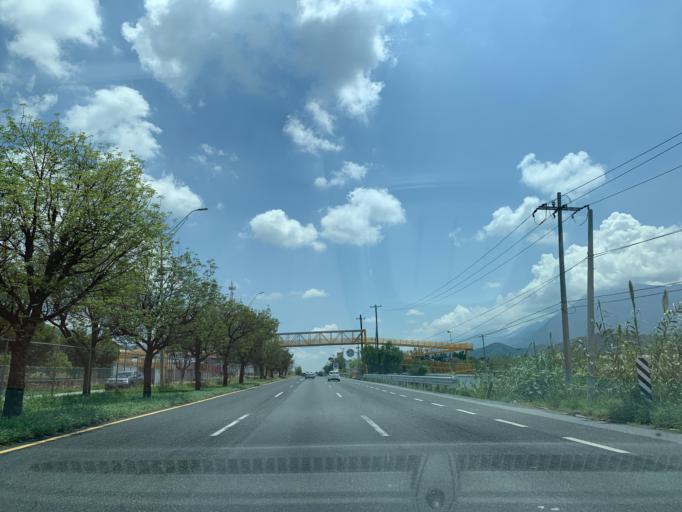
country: MX
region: Nuevo Leon
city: Santiago
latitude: 25.3913
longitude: -100.1197
